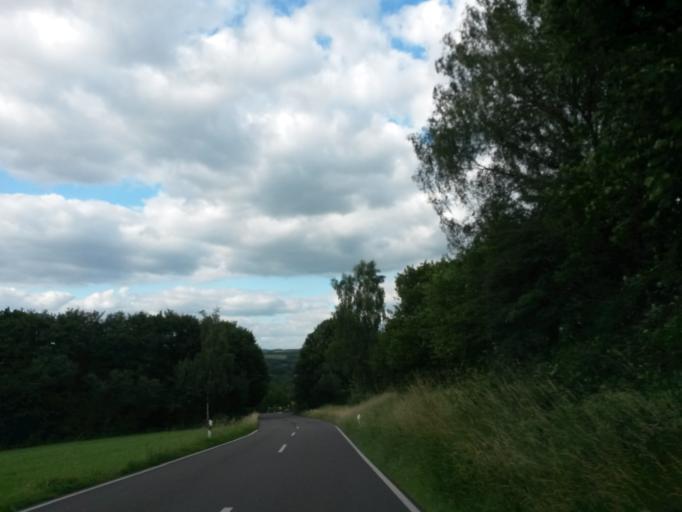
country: DE
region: North Rhine-Westphalia
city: Waldbrol
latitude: 50.9221
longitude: 7.6360
